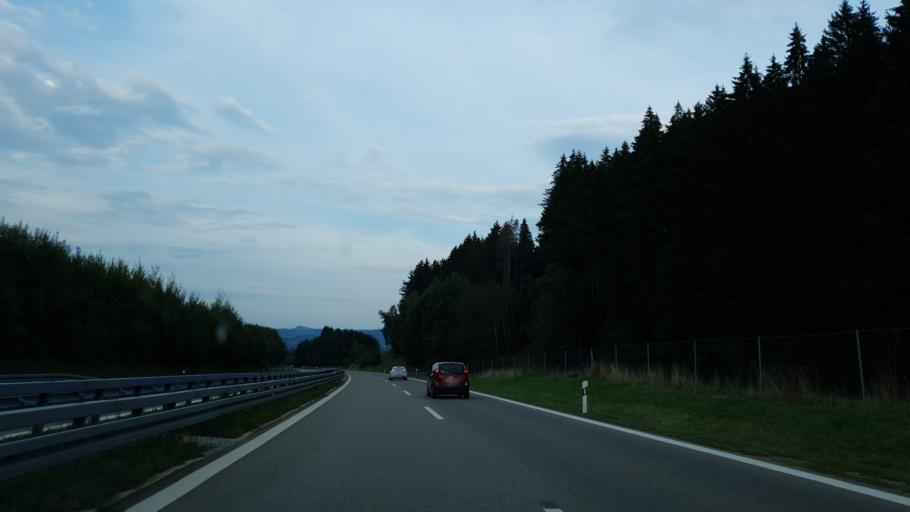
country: DE
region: Bavaria
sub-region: Swabia
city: Buchenberg
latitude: 47.6680
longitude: 10.2582
